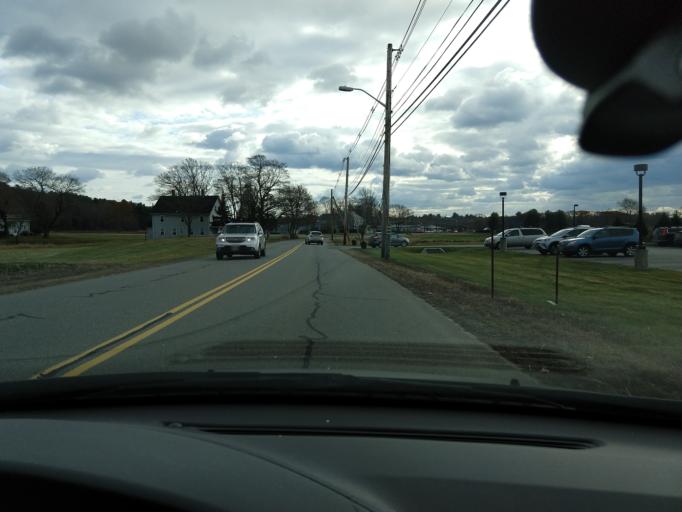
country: US
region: Massachusetts
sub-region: Middlesex County
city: West Concord
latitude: 42.4250
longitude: -71.3738
